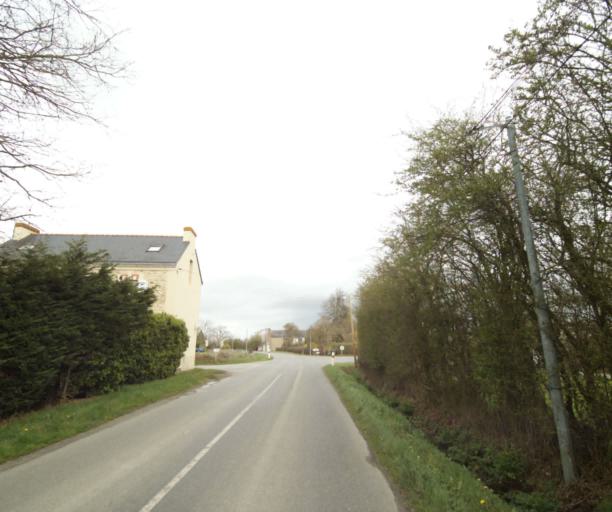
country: FR
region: Pays de la Loire
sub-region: Departement de la Loire-Atlantique
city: Bouvron
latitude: 47.4380
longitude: -1.8518
